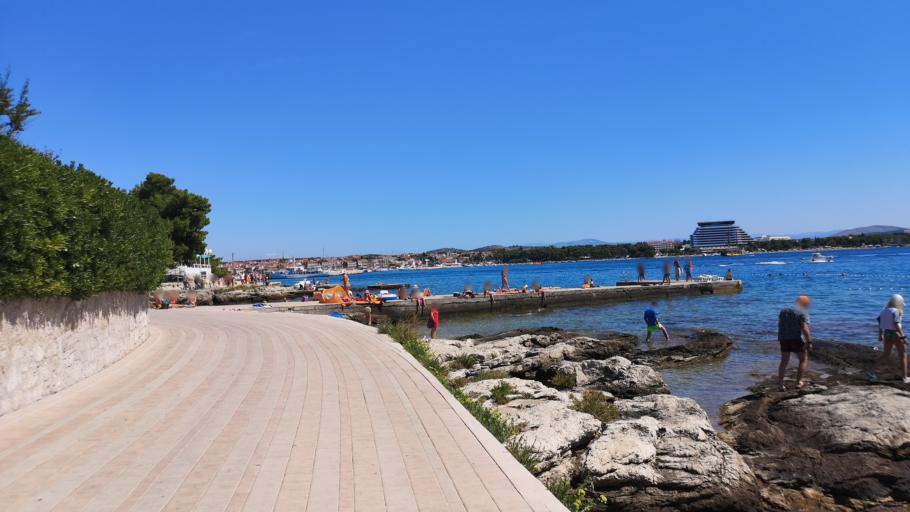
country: HR
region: Sibensko-Kniniska
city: Vodice
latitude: 43.7521
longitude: 15.7722
